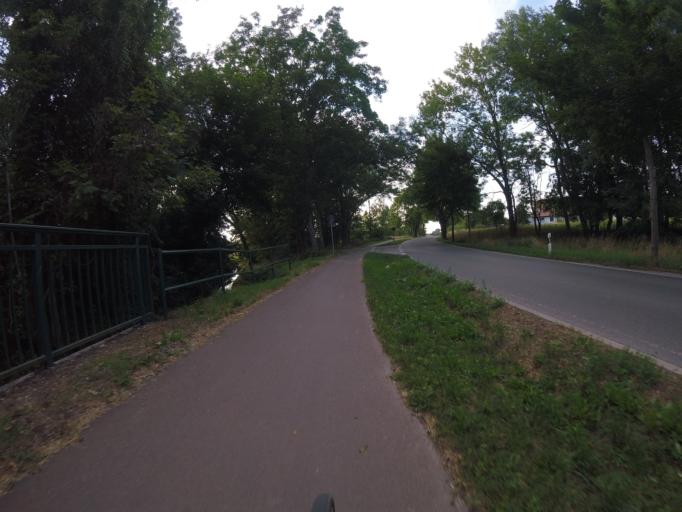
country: DE
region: Brandenburg
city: Altlandsberg
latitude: 52.5713
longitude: 13.7175
